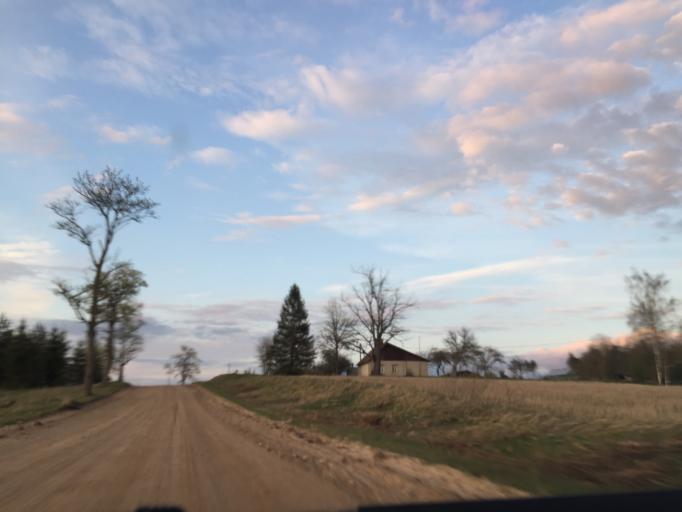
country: LV
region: Gulbenes Rajons
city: Gulbene
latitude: 57.2610
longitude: 26.9234
